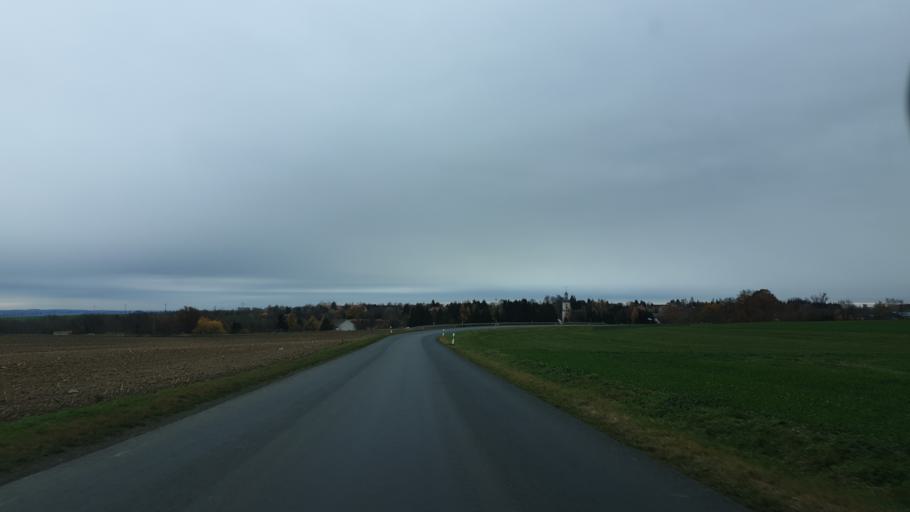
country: DE
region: Thuringia
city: Rauda
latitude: 50.9828
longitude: 11.9402
